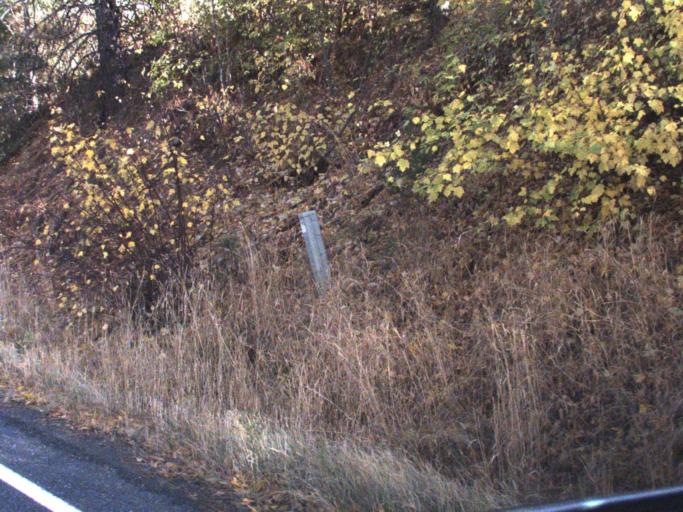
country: US
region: Washington
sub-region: Stevens County
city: Kettle Falls
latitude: 48.6694
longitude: -118.0389
